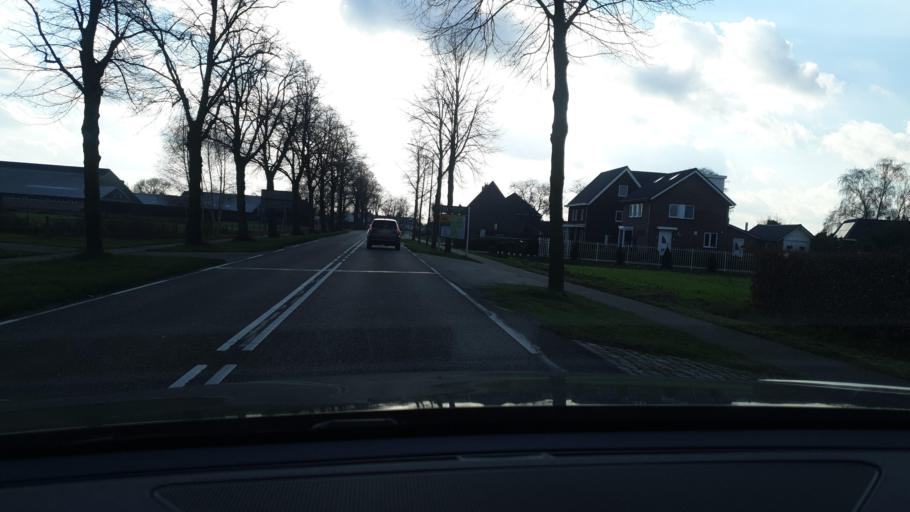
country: NL
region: North Brabant
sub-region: Gemeente Valkenswaard
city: Valkenswaard
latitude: 51.3404
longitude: 5.4131
